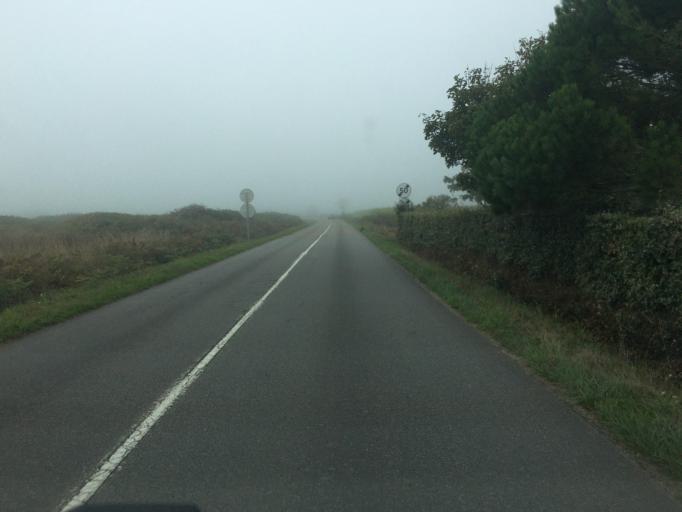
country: FR
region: Brittany
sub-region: Departement du Finistere
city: Plogoff
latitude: 48.0631
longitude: -4.6319
